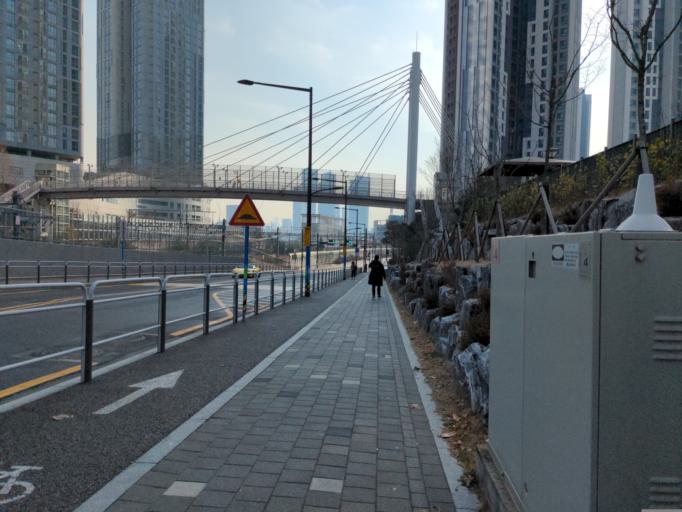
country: KR
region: Seoul
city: Seoul
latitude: 37.5576
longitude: 127.0389
